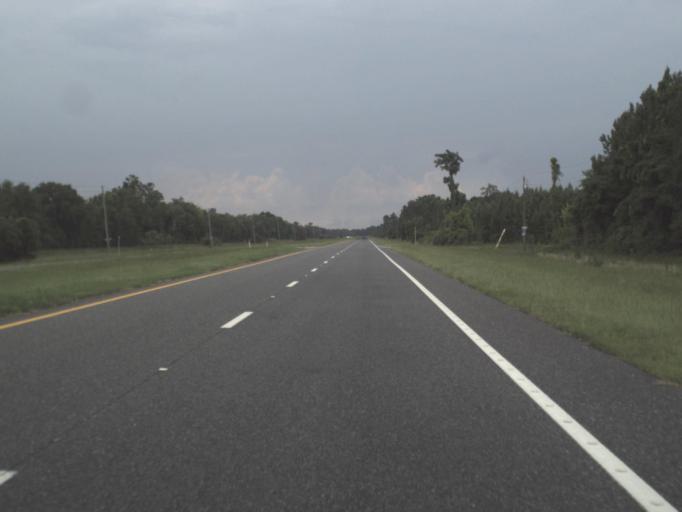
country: US
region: Florida
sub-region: Levy County
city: Inglis
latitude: 29.2060
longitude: -82.6946
